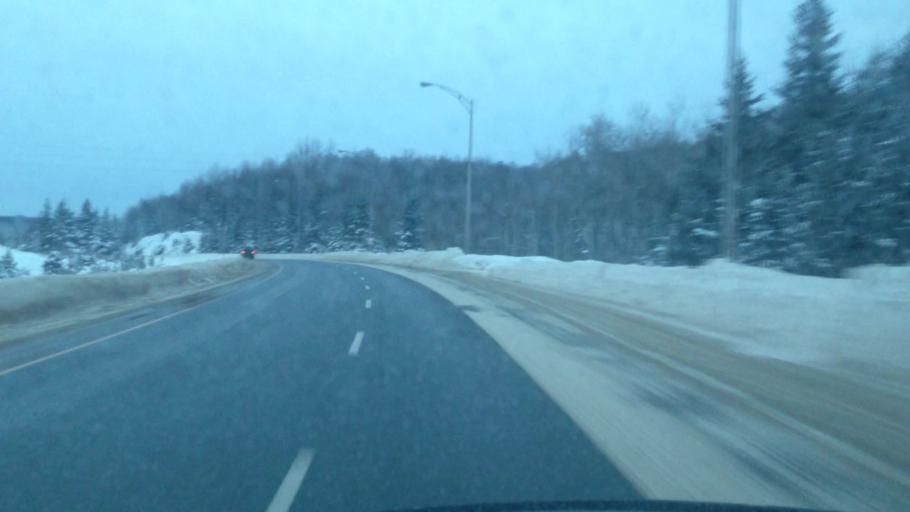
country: CA
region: Quebec
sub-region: Laurentides
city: Mont-Tremblant
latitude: 46.1156
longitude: -74.4664
